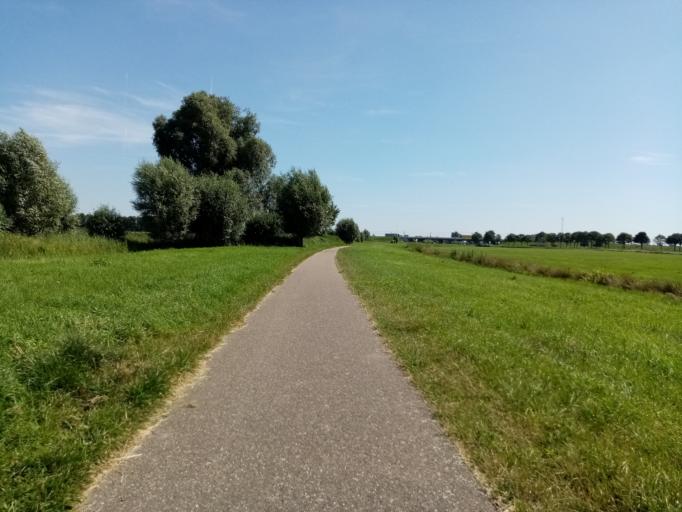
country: NL
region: North Brabant
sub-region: Gemeente Breda
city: Breda
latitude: 51.6363
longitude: 4.6889
